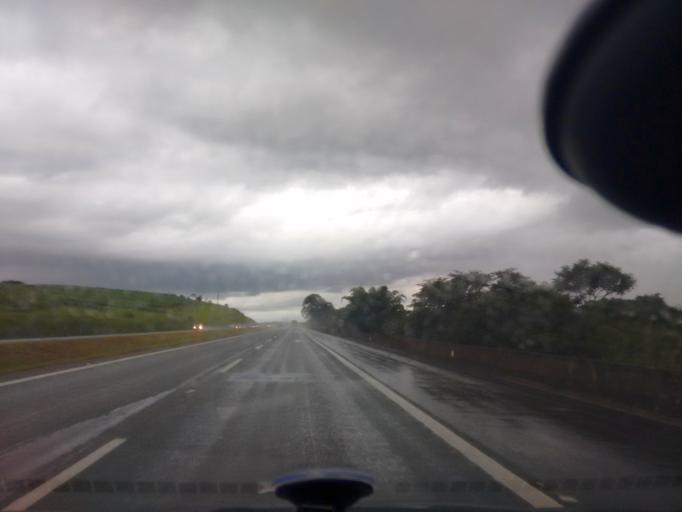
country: BR
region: Sao Paulo
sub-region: Iracemapolis
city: Iracemapolis
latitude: -22.6554
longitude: -47.4493
